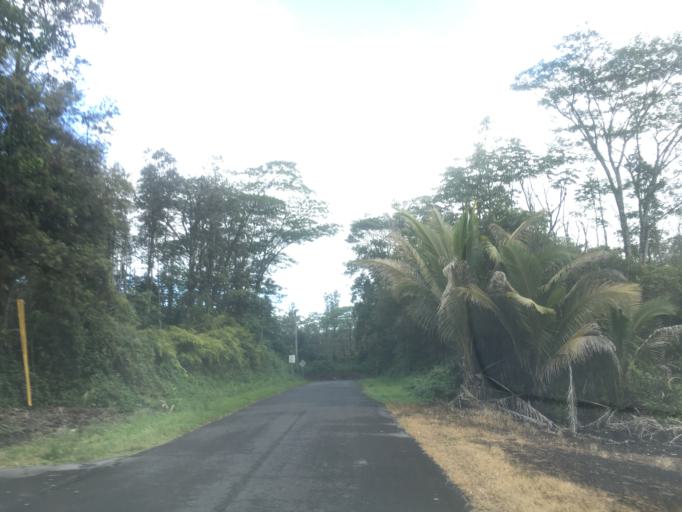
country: US
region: Hawaii
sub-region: Hawaii County
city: Leilani Estates
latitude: 19.4872
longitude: -154.9246
